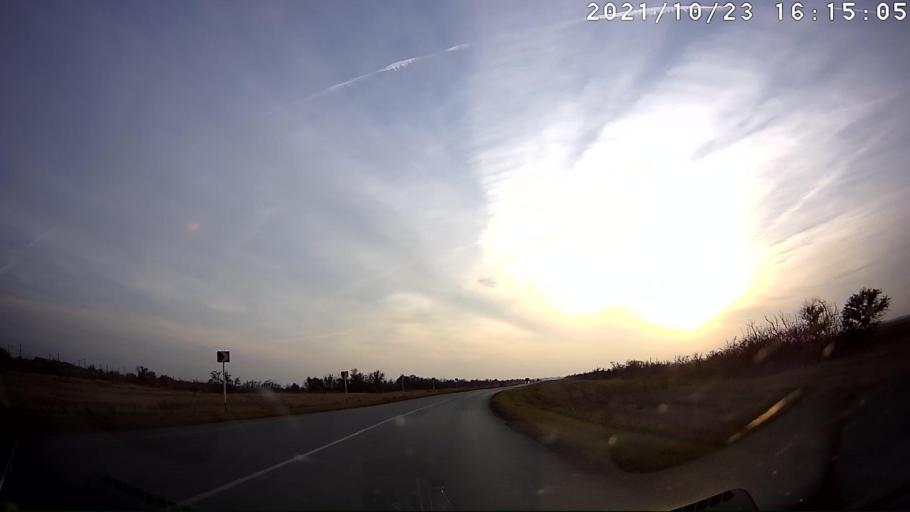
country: RU
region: Volgograd
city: Kotel'nikovo
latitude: 47.9377
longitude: 43.5995
